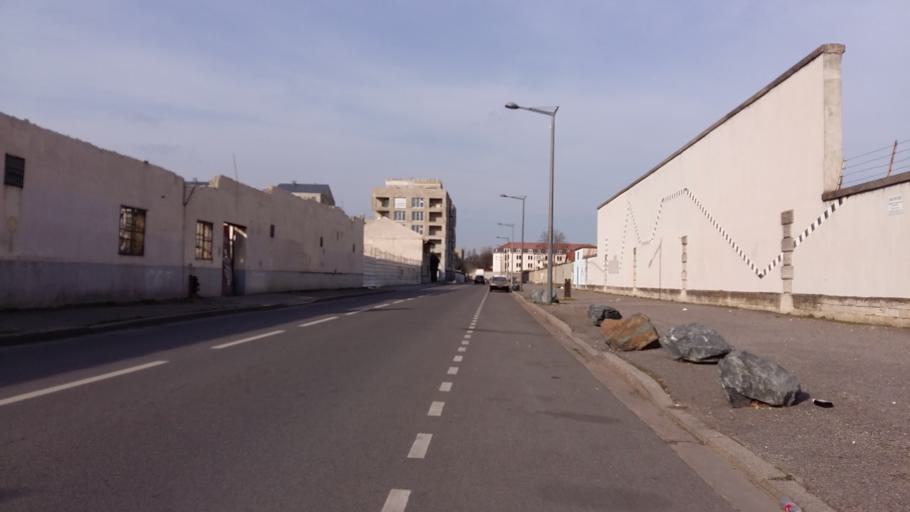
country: FR
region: Rhone-Alpes
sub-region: Departement du Rhone
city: Lyon
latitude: 45.7326
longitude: 4.8425
